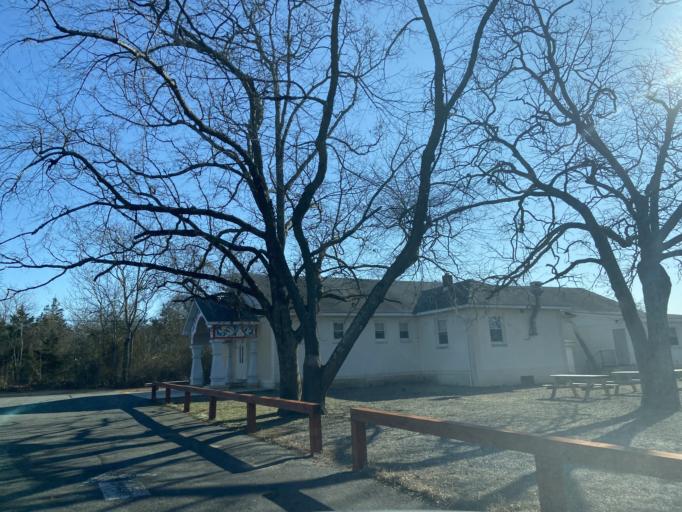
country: US
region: New Jersey
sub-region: Cumberland County
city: Vineland
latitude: 39.4871
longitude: -75.0674
